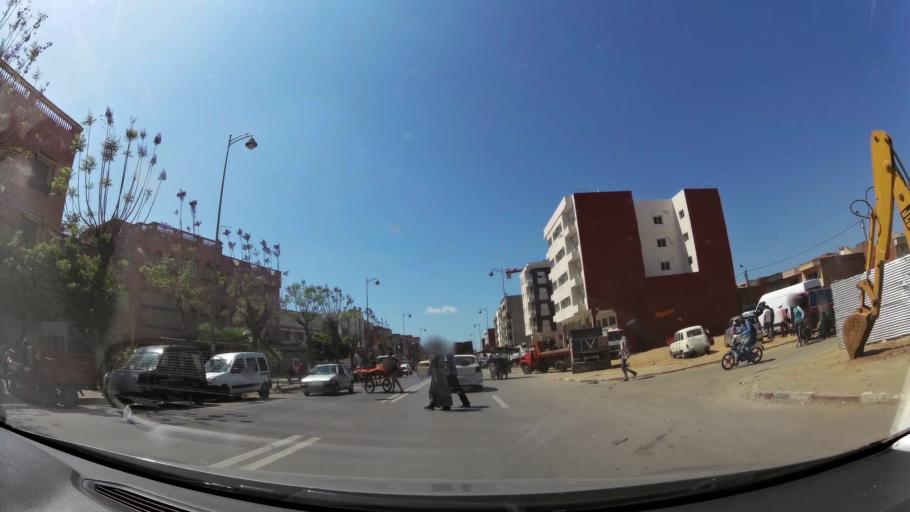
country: MA
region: Gharb-Chrarda-Beni Hssen
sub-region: Kenitra Province
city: Kenitra
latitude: 34.2418
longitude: -6.5489
